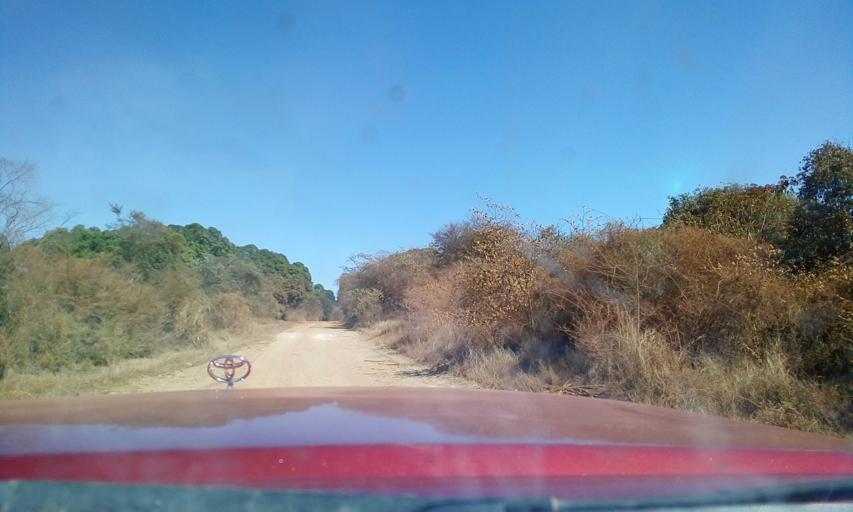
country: MG
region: Boeny
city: Mahajanga
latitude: -15.9613
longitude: 45.9629
